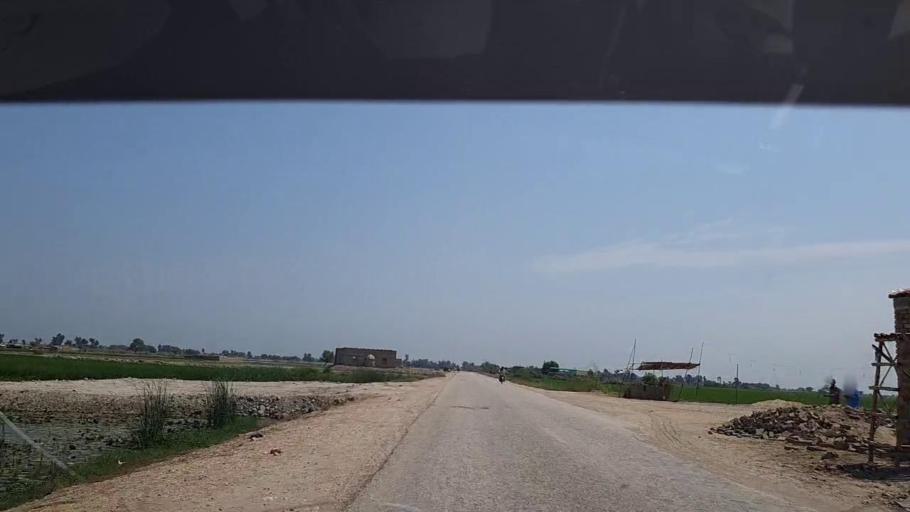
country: PK
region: Sindh
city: Rustam jo Goth
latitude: 28.0854
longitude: 68.7915
